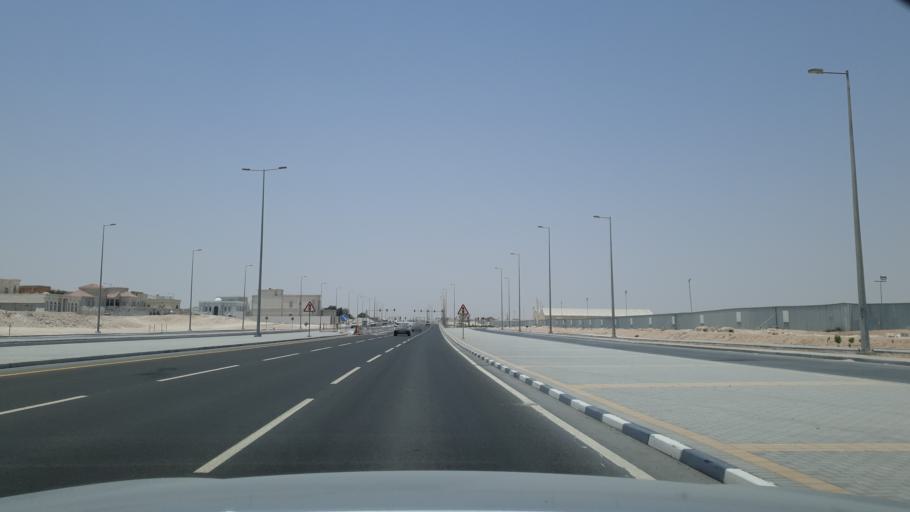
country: QA
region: Baladiyat Umm Salal
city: Umm Salal Muhammad
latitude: 25.4169
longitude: 51.4474
